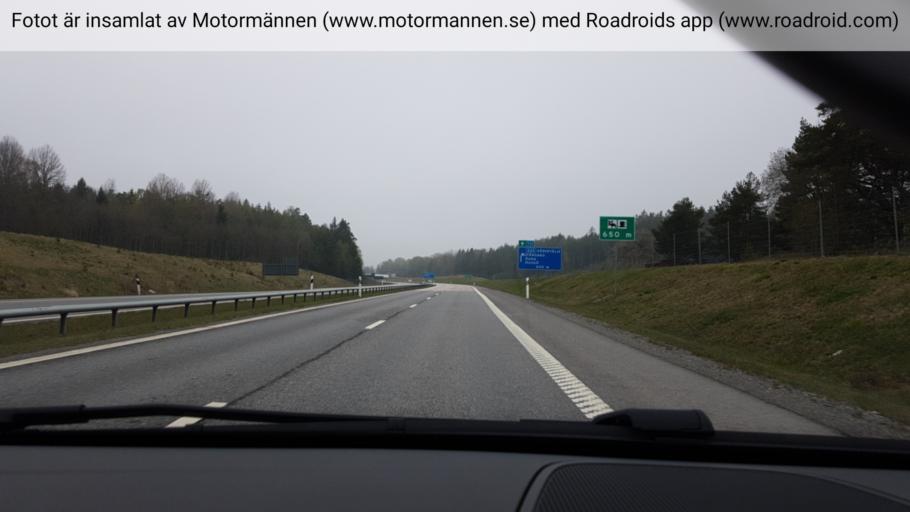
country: SE
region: Stockholm
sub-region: Nynashamns Kommun
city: Osmo
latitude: 58.9877
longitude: 17.9237
